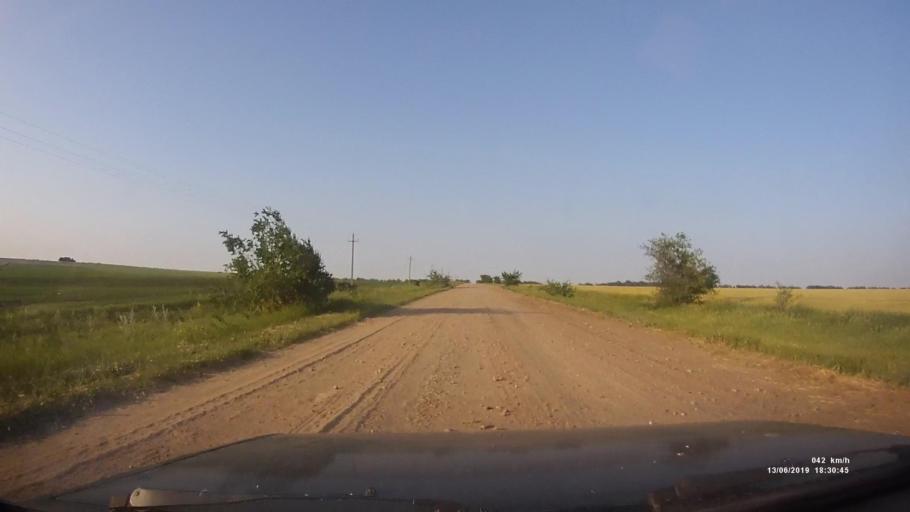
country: RU
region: Rostov
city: Kazanskaya
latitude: 49.8631
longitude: 41.3527
